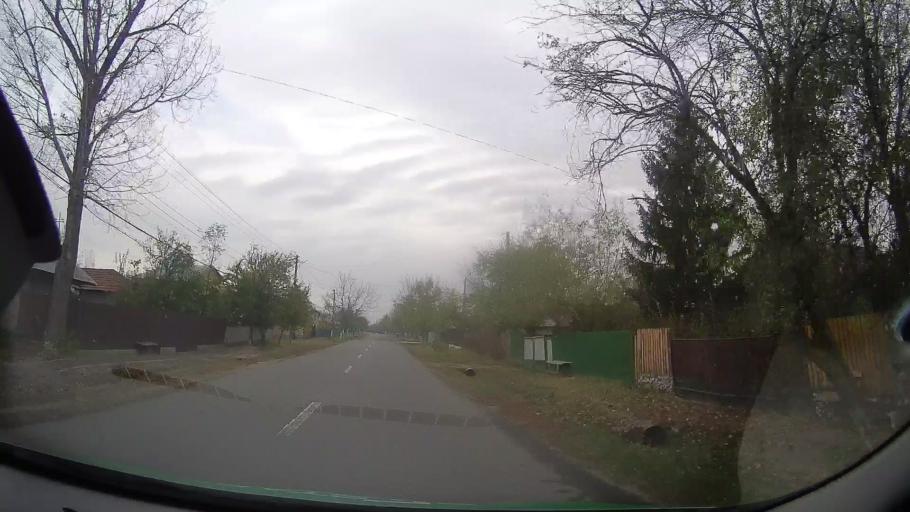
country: RO
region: Prahova
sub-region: Comuna Valea Calugareasca
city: Pantazi
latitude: 44.9193
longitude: 26.1559
